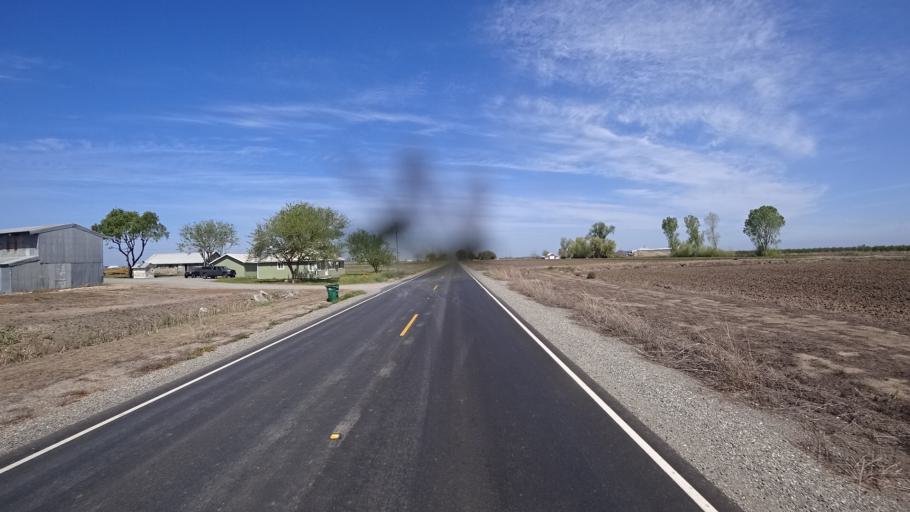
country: US
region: California
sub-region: Glenn County
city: Hamilton City
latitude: 39.6120
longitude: -122.0650
